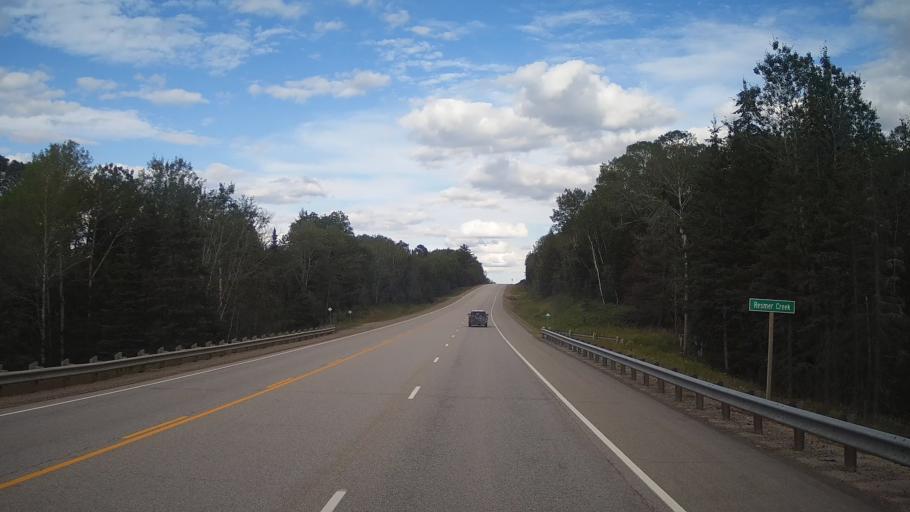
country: CA
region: Ontario
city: Mattawa
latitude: 46.2807
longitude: -78.4292
